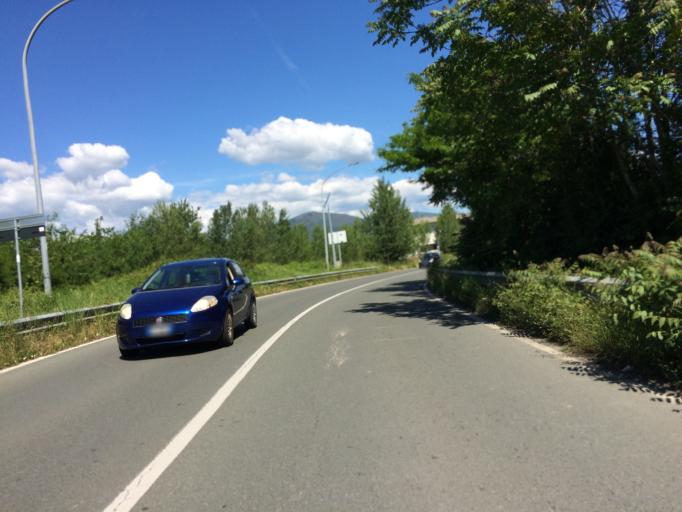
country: IT
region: Tuscany
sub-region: Provincia di Massa-Carrara
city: Terrarossa
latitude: 44.2269
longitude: 9.9663
